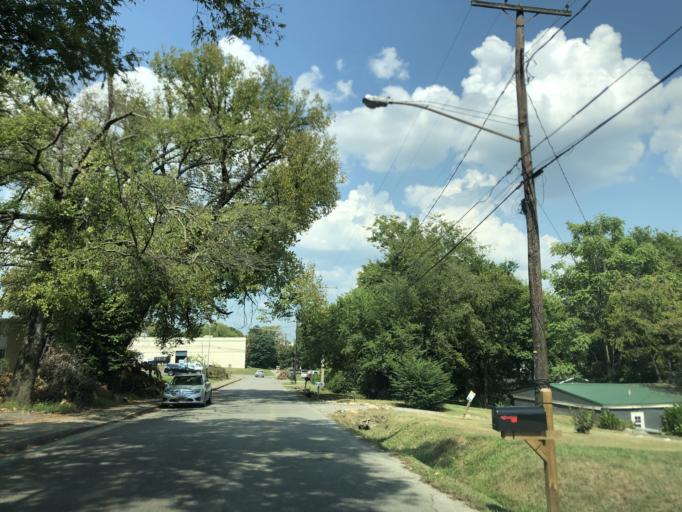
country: US
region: Tennessee
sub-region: Davidson County
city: Oak Hill
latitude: 36.1234
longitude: -86.7561
